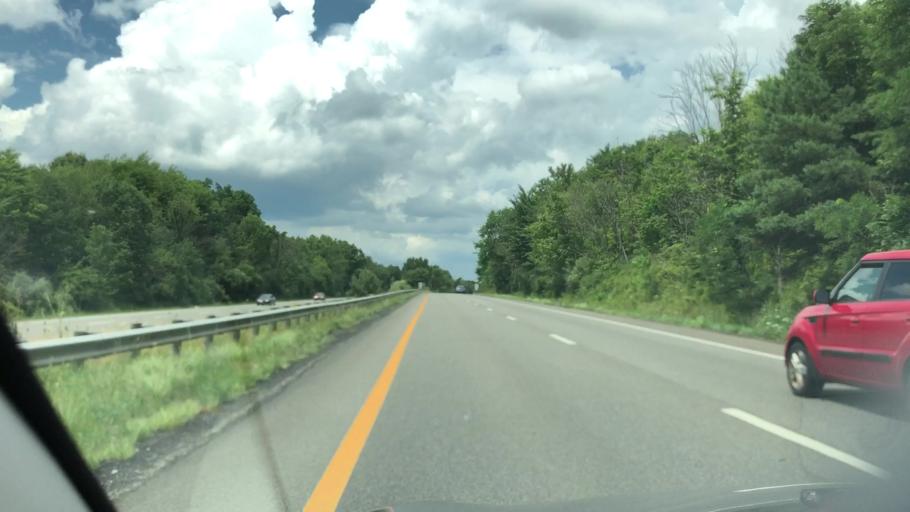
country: US
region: Ohio
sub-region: Summit County
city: Norton
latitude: 41.0705
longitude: -81.6643
